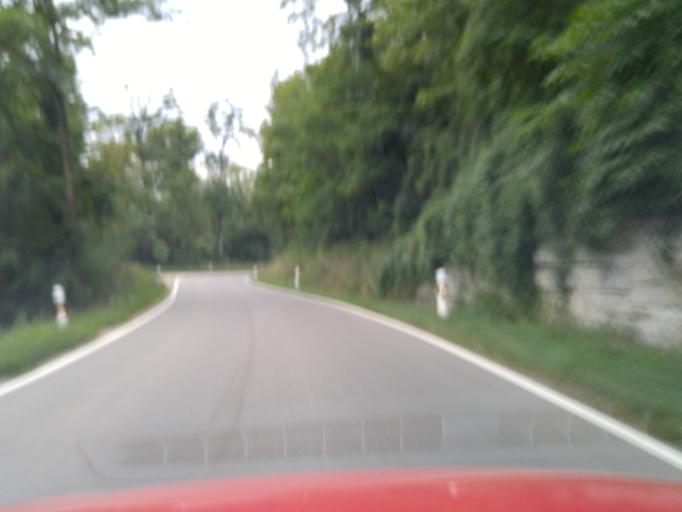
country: DE
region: Baden-Wuerttemberg
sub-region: Regierungsbezirk Stuttgart
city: Pfaffenhofen
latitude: 49.0250
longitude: 8.9767
